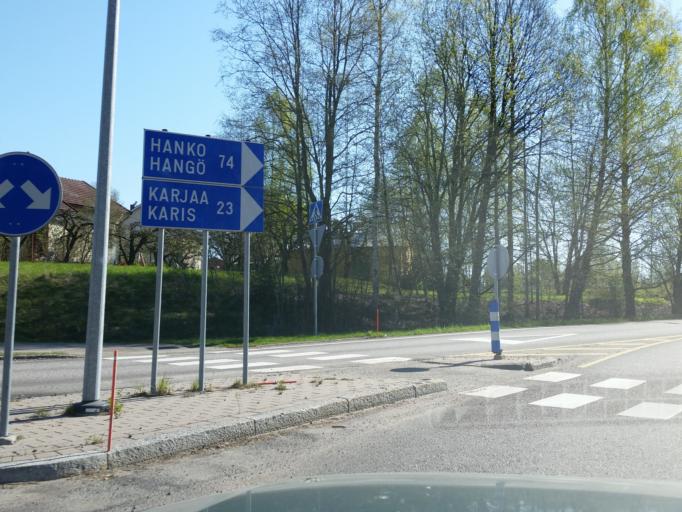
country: FI
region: Uusimaa
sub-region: Helsinki
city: Lohja
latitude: 60.1795
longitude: 23.9914
